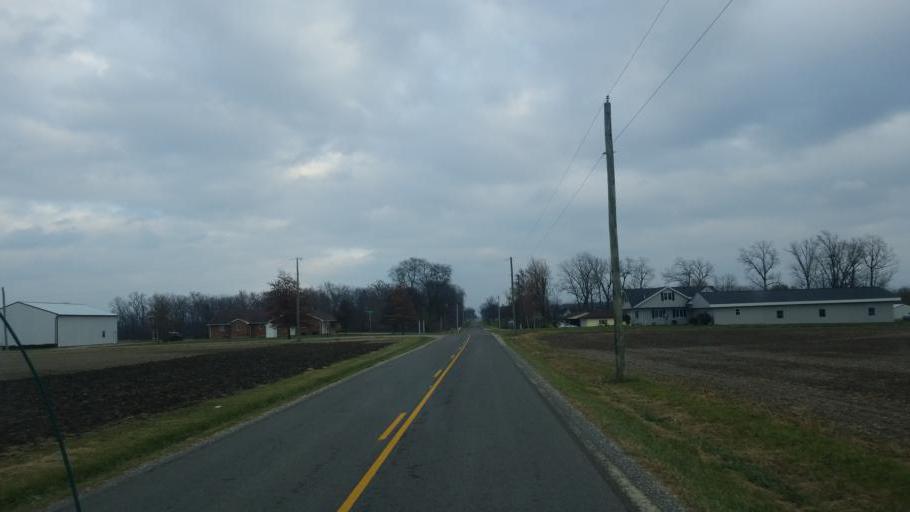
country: US
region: Ohio
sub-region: Mercer County
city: Coldwater
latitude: 40.5089
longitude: -84.6583
